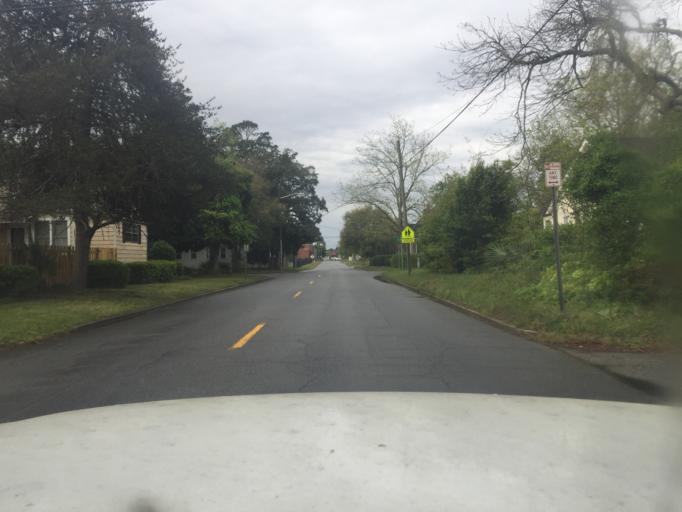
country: US
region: Georgia
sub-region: Chatham County
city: Thunderbolt
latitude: 32.0362
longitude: -81.0939
